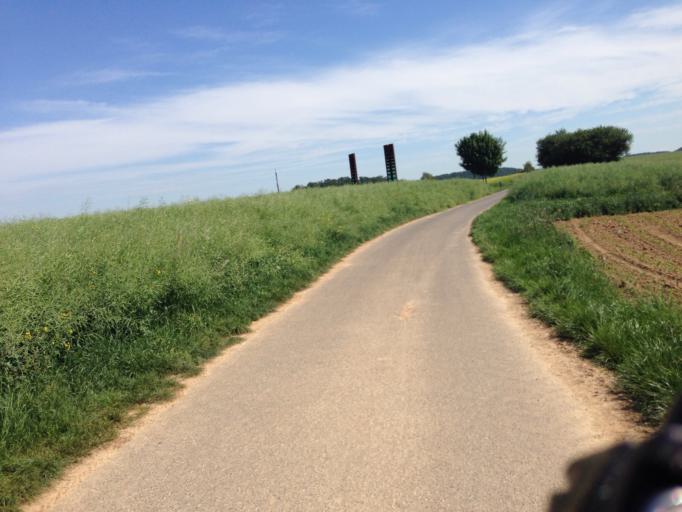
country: DE
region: Hesse
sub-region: Regierungsbezirk Darmstadt
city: Hammersbach
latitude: 50.2305
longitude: 9.0015
